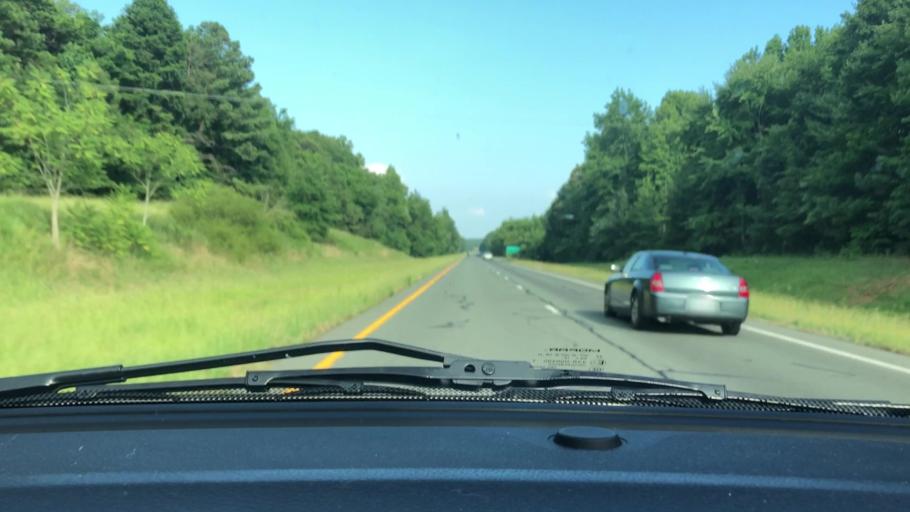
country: US
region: North Carolina
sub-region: Chatham County
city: Siler City
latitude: 35.7748
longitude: -79.4967
